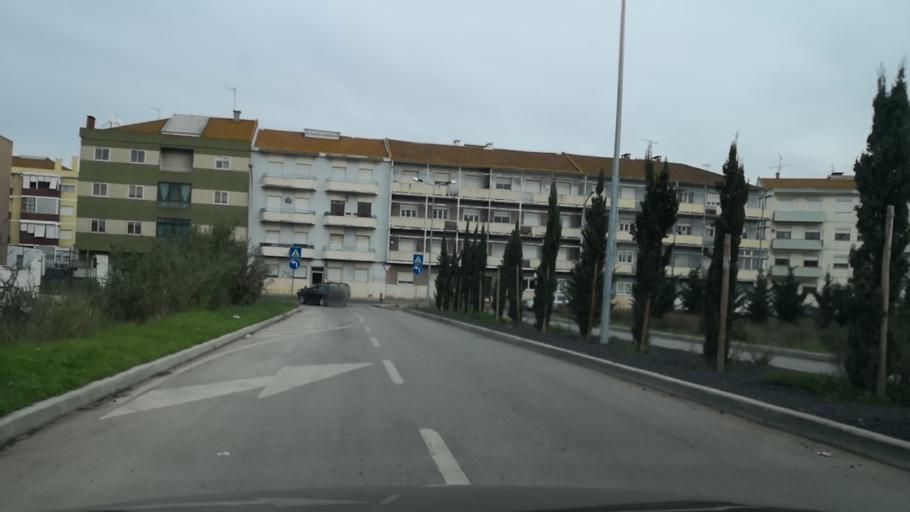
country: PT
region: Setubal
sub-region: Setubal
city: Setubal
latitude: 38.5343
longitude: -8.8849
